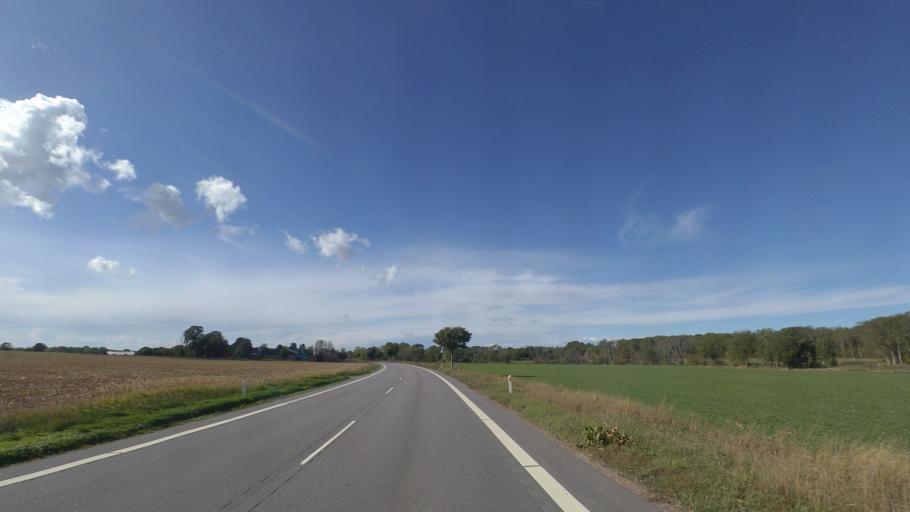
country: DK
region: Capital Region
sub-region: Bornholm Kommune
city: Ronne
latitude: 55.0738
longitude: 14.7969
